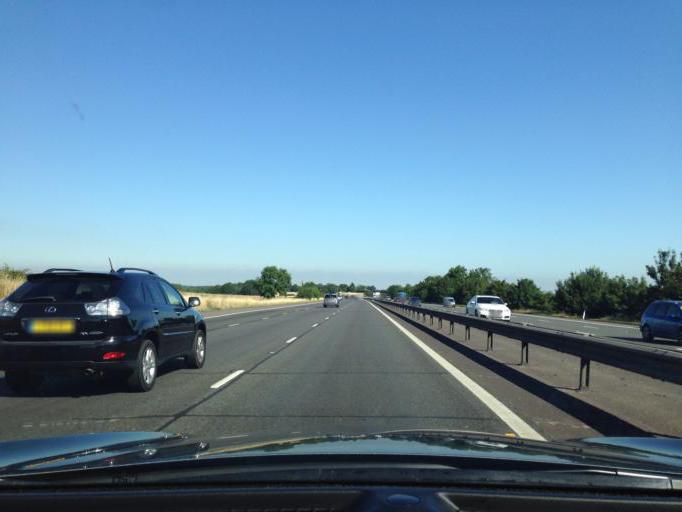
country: GB
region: England
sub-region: Oxfordshire
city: Watlington
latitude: 51.6881
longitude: -0.9781
